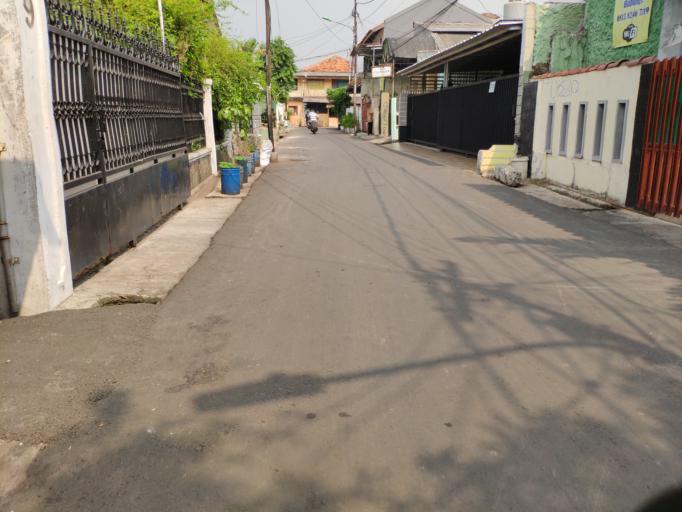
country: ID
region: Jakarta Raya
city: Jakarta
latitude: -6.1955
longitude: 106.8652
